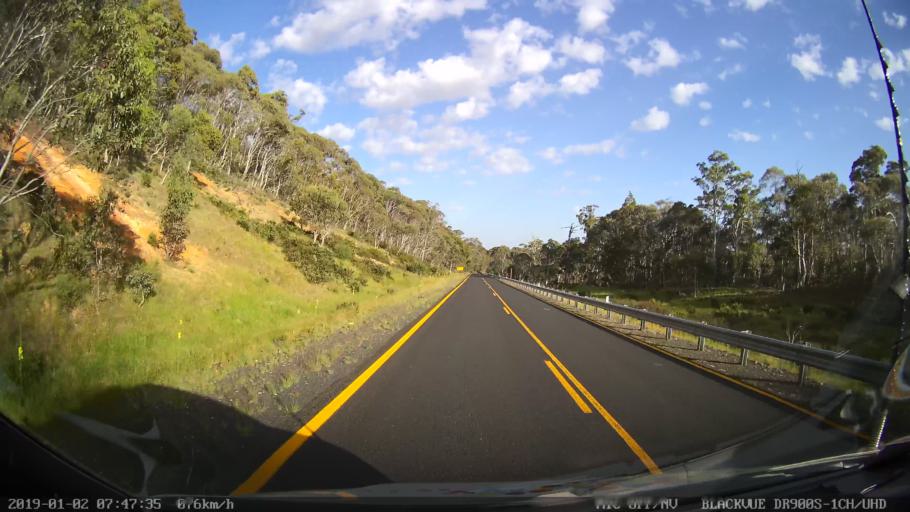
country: AU
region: New South Wales
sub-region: Tumut Shire
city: Tumut
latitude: -35.7633
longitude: 148.5196
